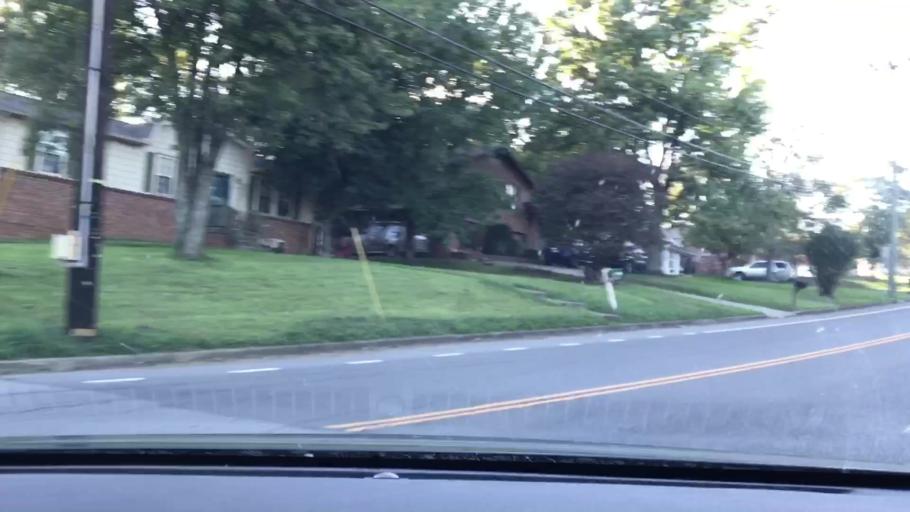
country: US
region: Tennessee
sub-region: Williamson County
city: Brentwood Estates
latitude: 36.0569
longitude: -86.7001
